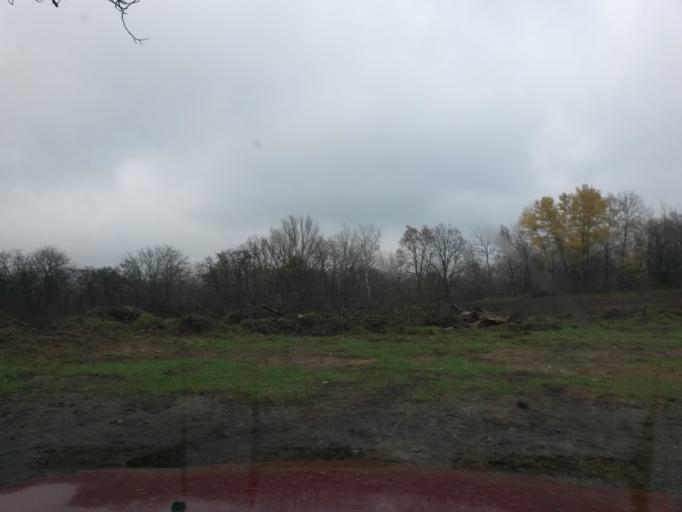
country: SK
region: Kosicky
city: Cierna nad Tisou
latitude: 48.5239
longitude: 21.9585
